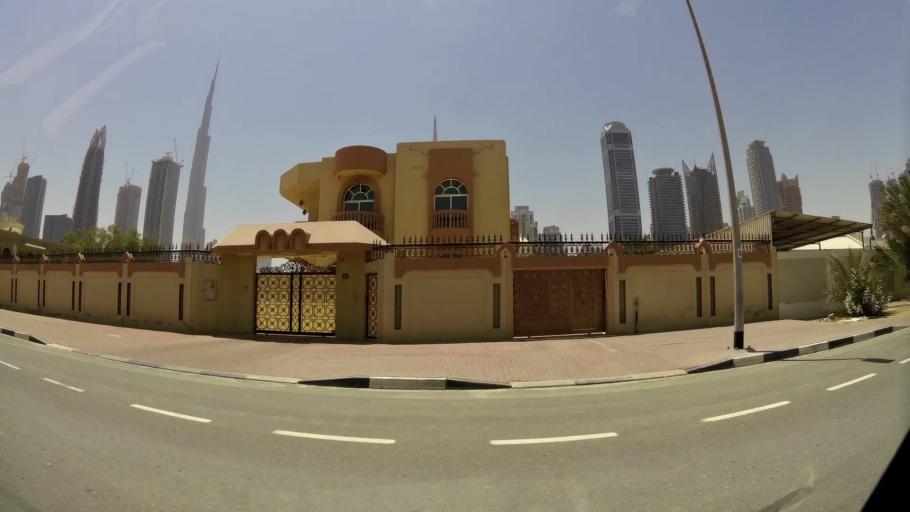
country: AE
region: Dubai
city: Dubai
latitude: 25.1980
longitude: 55.2611
